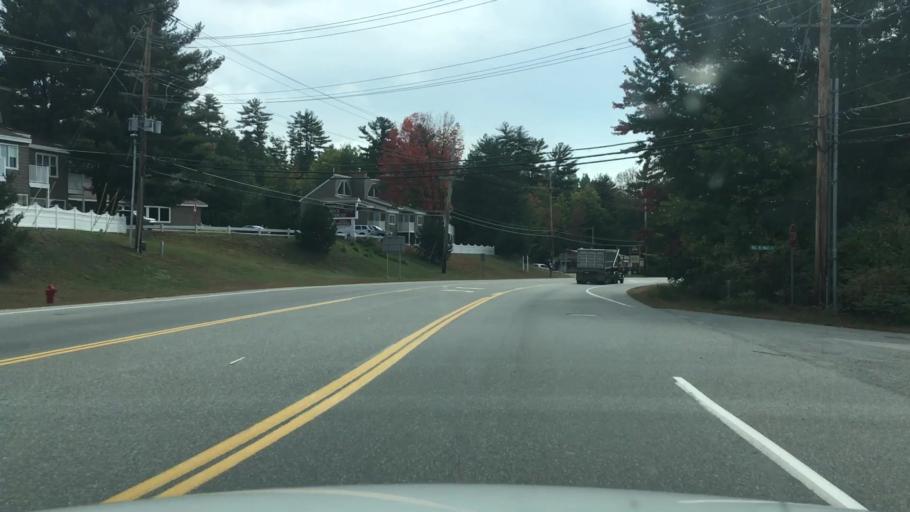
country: US
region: New Hampshire
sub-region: Carroll County
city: North Conway
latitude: 44.0780
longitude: -71.1392
